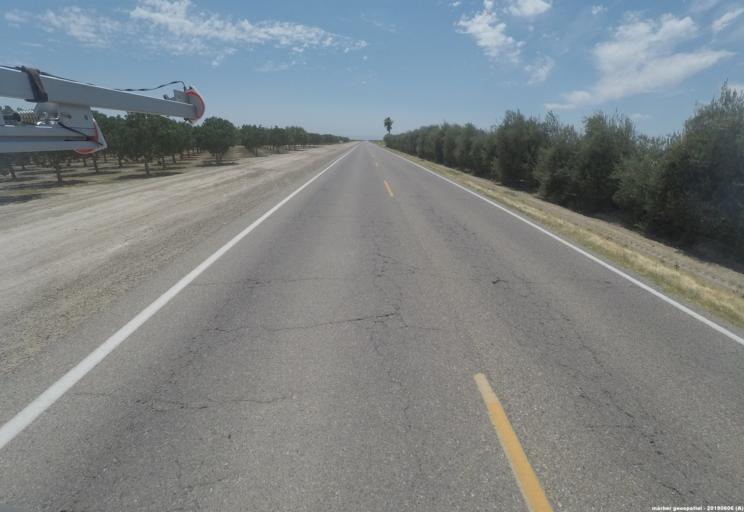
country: US
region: California
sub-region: Fresno County
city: Mendota
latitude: 36.8588
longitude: -120.3442
